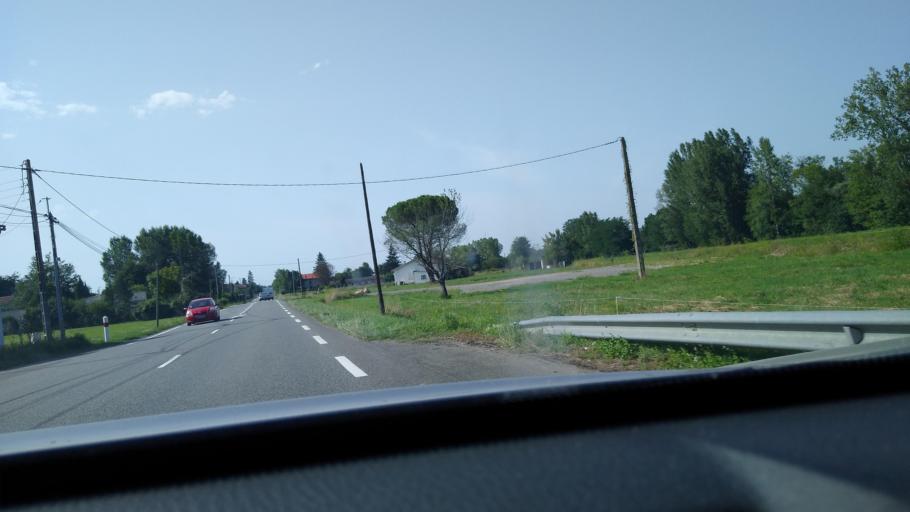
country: FR
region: Midi-Pyrenees
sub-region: Departement de la Haute-Garonne
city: Salies-du-Salat
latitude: 43.0510
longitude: 0.9832
